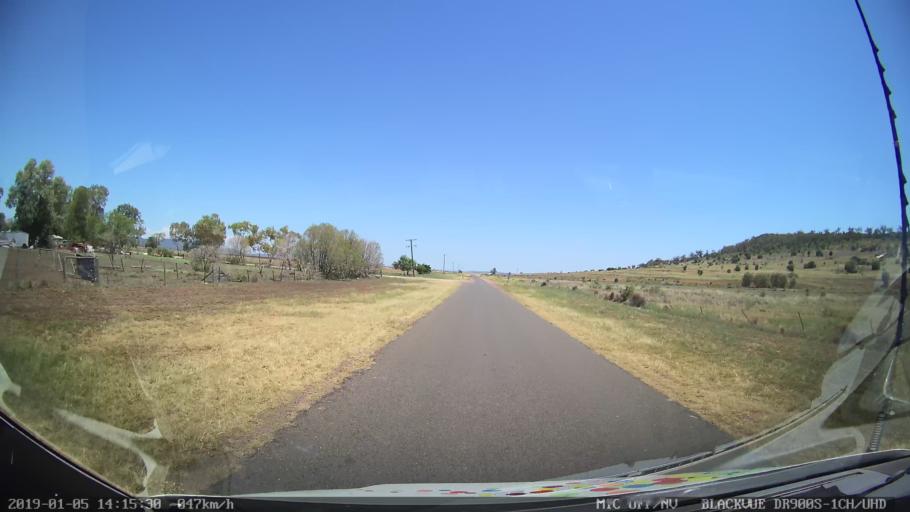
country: AU
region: New South Wales
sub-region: Liverpool Plains
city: Quirindi
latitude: -31.2480
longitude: 150.4709
